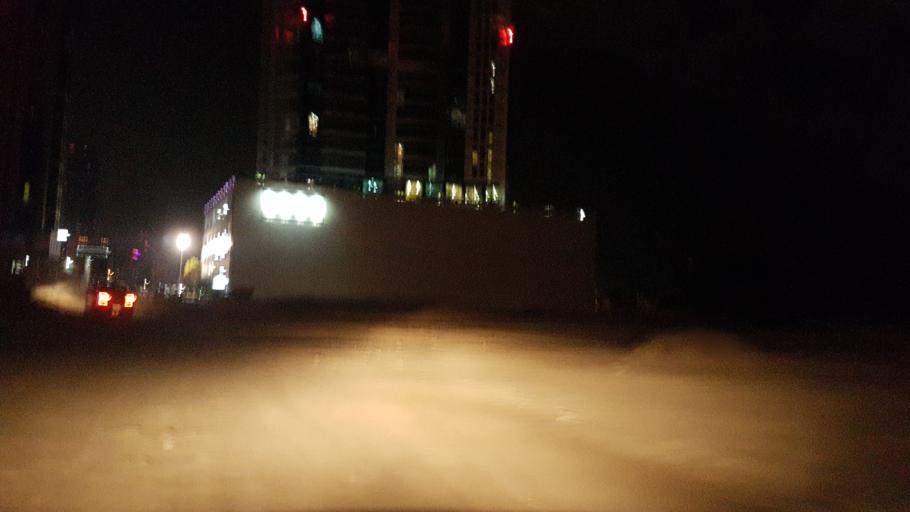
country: BH
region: Manama
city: Jidd Hafs
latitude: 26.2364
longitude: 50.5513
